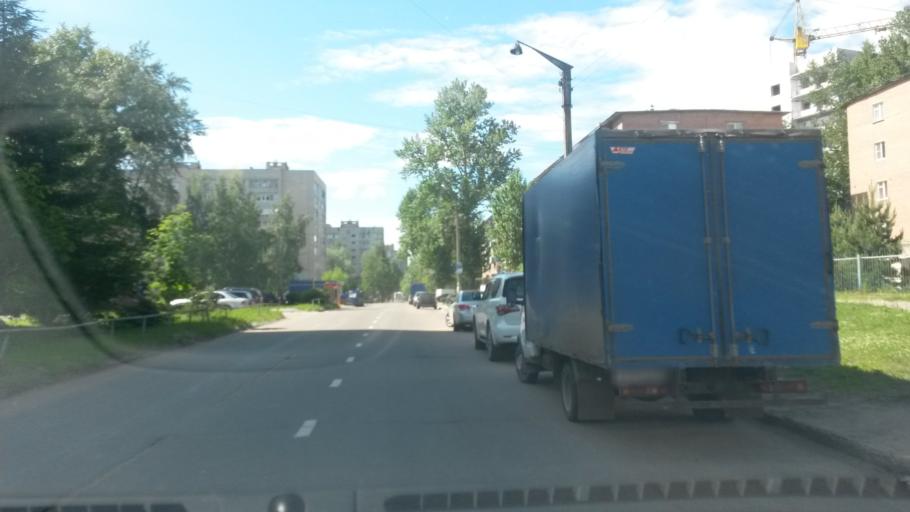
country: RU
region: Jaroslavl
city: Yaroslavl
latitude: 57.5821
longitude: 39.8313
